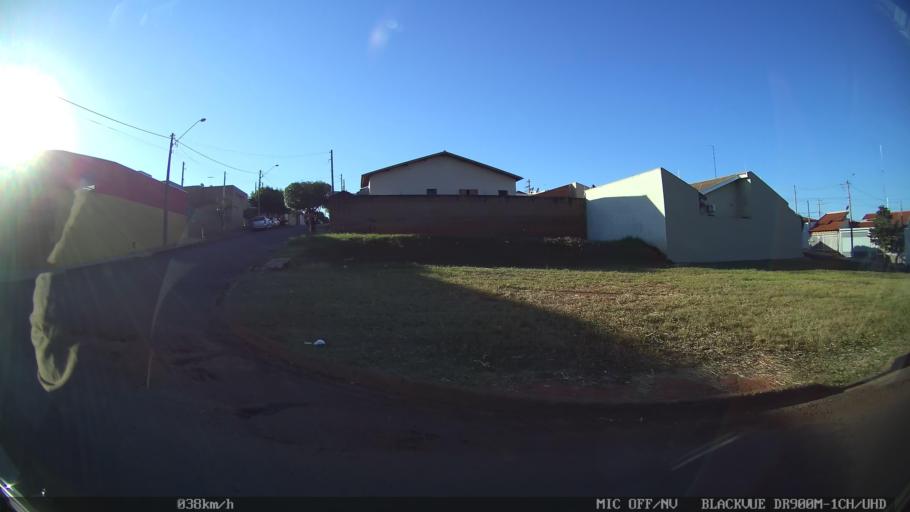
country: BR
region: Sao Paulo
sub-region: Guapiacu
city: Guapiacu
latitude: -20.7931
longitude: -49.2324
